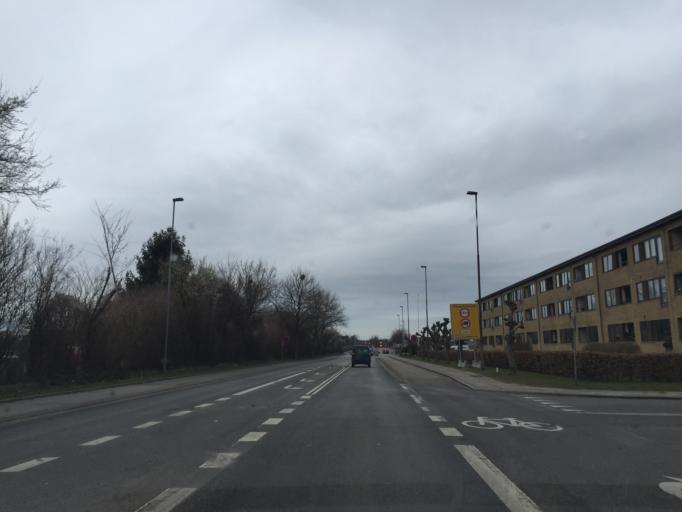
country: DK
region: South Denmark
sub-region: Odense Kommune
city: Odense
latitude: 55.4045
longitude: 10.3400
